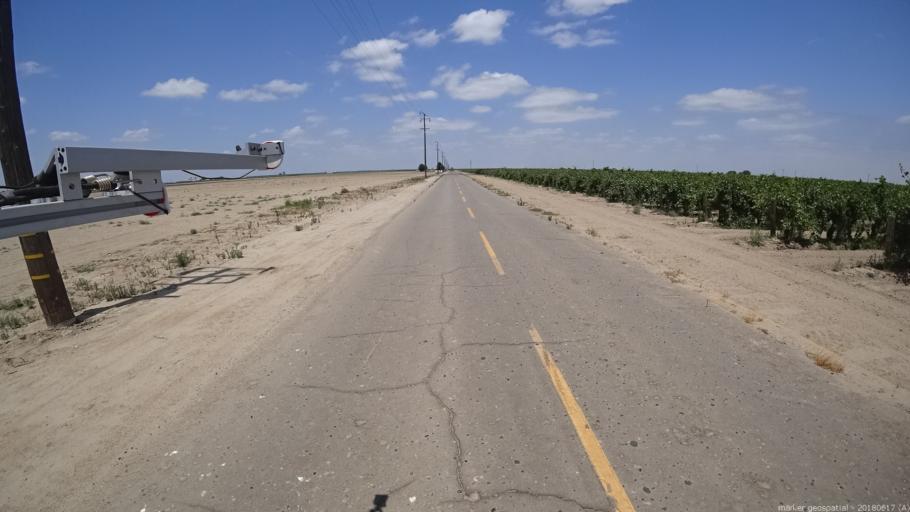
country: US
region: California
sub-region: Fresno County
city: Biola
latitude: 36.8262
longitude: -120.1150
